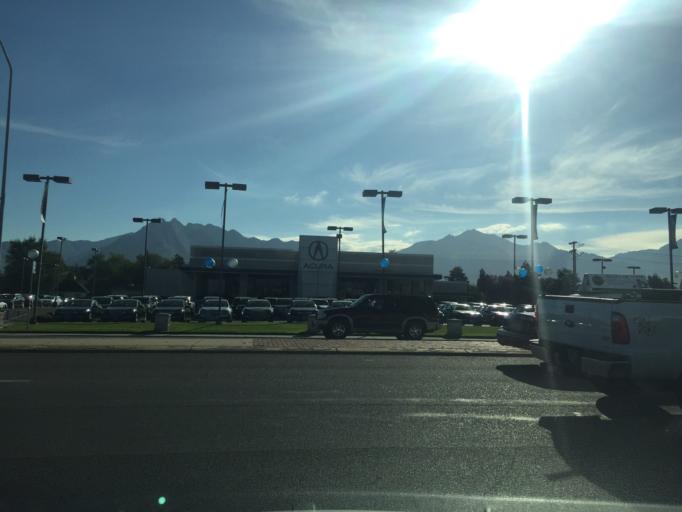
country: US
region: Utah
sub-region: Salt Lake County
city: Murray
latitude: 40.6487
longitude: -111.8888
